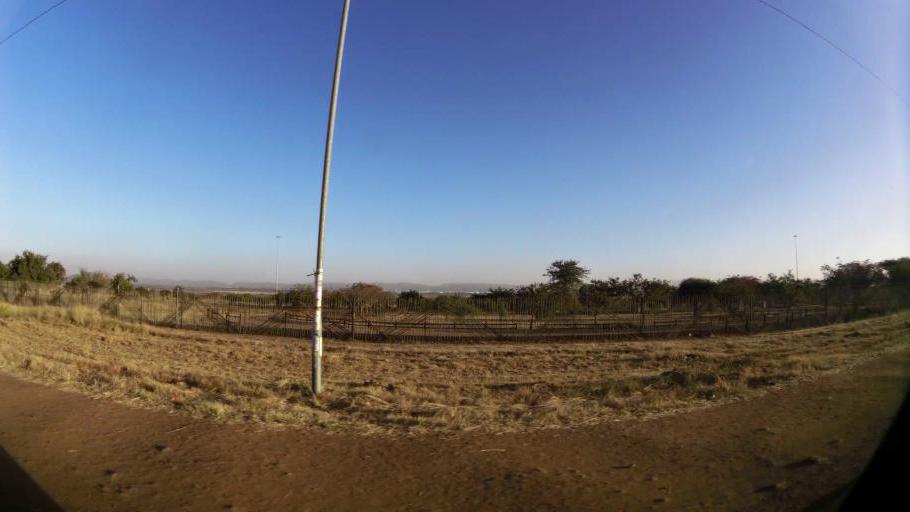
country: ZA
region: Gauteng
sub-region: City of Tshwane Metropolitan Municipality
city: Mabopane
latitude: -25.5785
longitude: 28.0941
